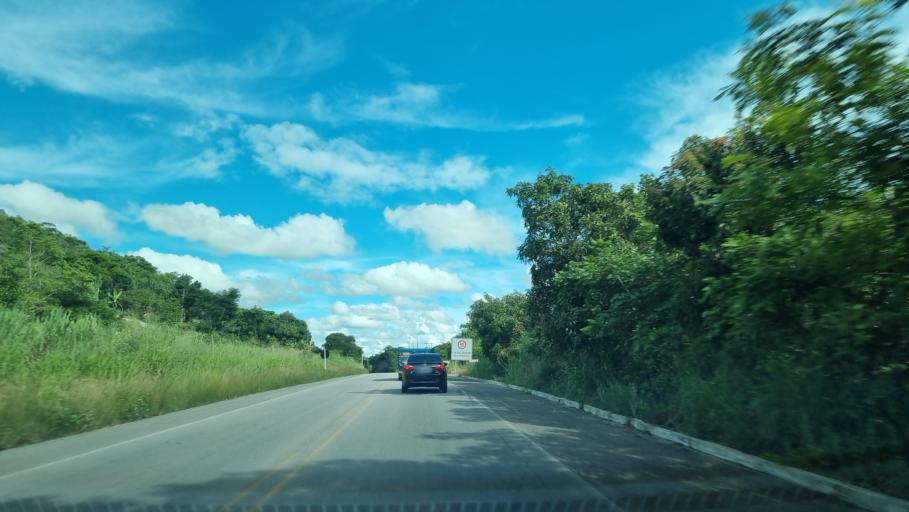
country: BR
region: Pernambuco
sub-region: Agrestina
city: Agrestina
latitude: -8.3814
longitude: -35.9830
